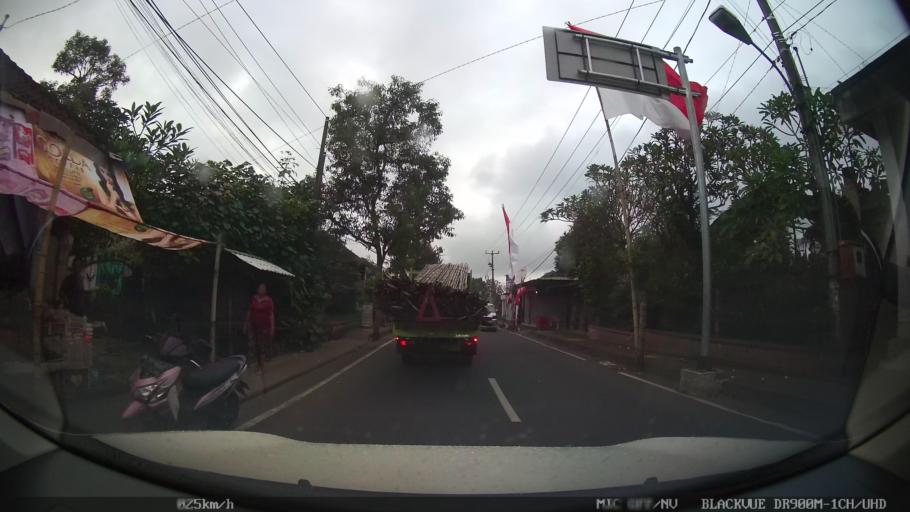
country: ID
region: Bali
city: Badung
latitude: -8.4285
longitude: 115.2459
